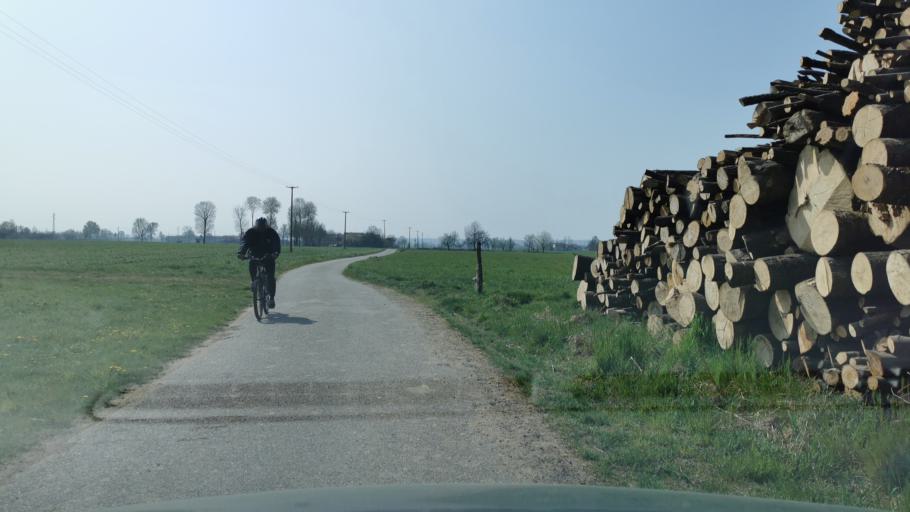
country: IT
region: Piedmont
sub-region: Provincia di Torino
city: Favria
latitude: 45.3217
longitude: 7.6974
